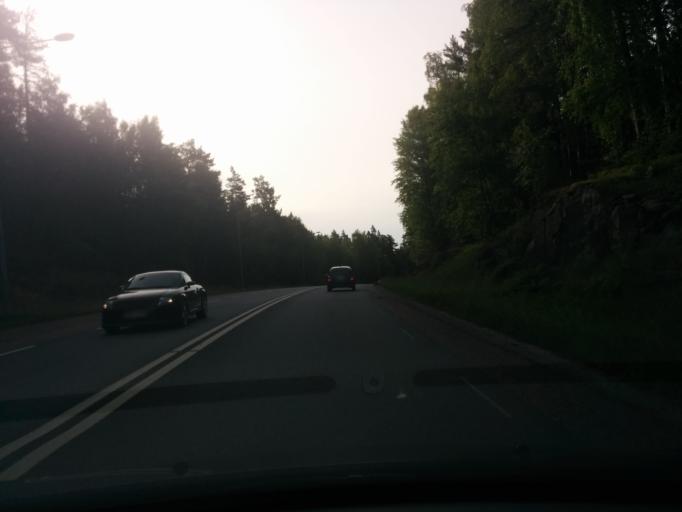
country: SE
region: Stockholm
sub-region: Sollentuna Kommun
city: Sollentuna
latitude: 59.4412
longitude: 17.9804
